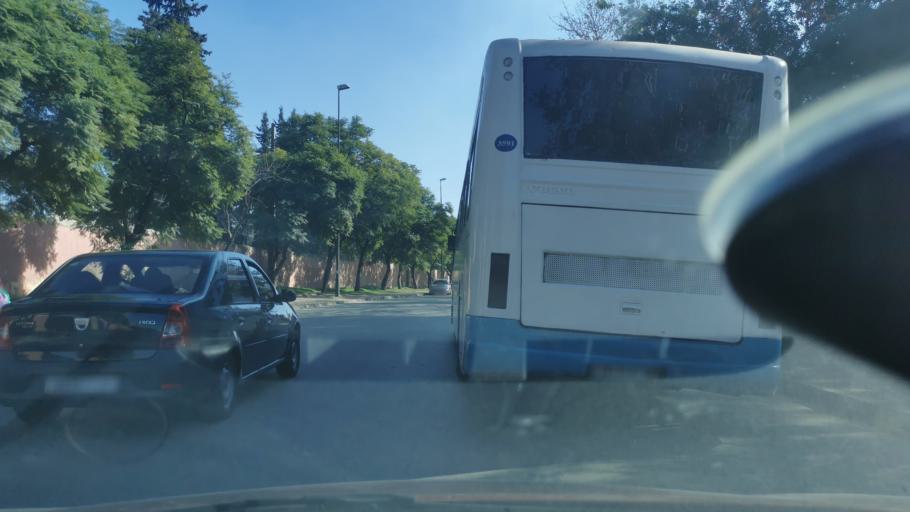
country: MA
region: Fes-Boulemane
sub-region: Fes
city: Fes
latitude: 34.0313
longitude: -4.9850
